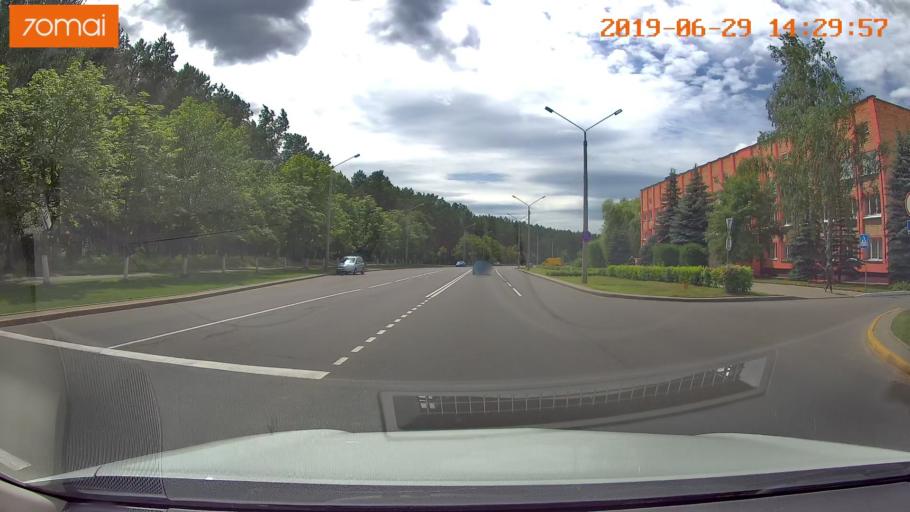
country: BY
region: Minsk
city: Salihorsk
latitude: 52.7819
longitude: 27.5240
